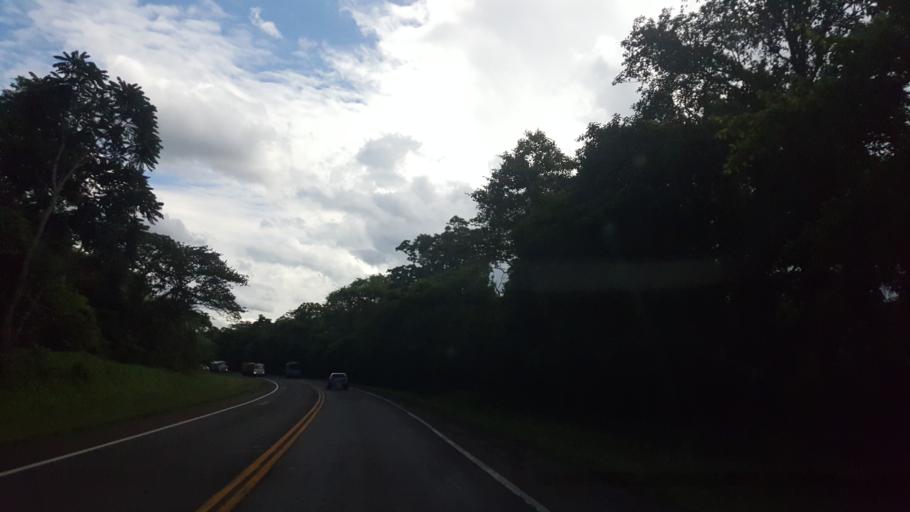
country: AR
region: Misiones
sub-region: Departamento de Iguazu
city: Puerto Iguazu
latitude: -25.6899
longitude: -54.5142
